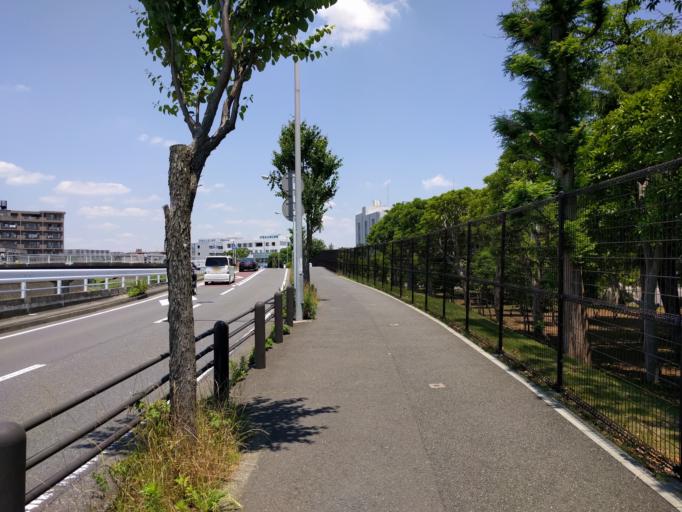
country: JP
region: Kanagawa
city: Fujisawa
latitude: 35.4027
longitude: 139.5378
